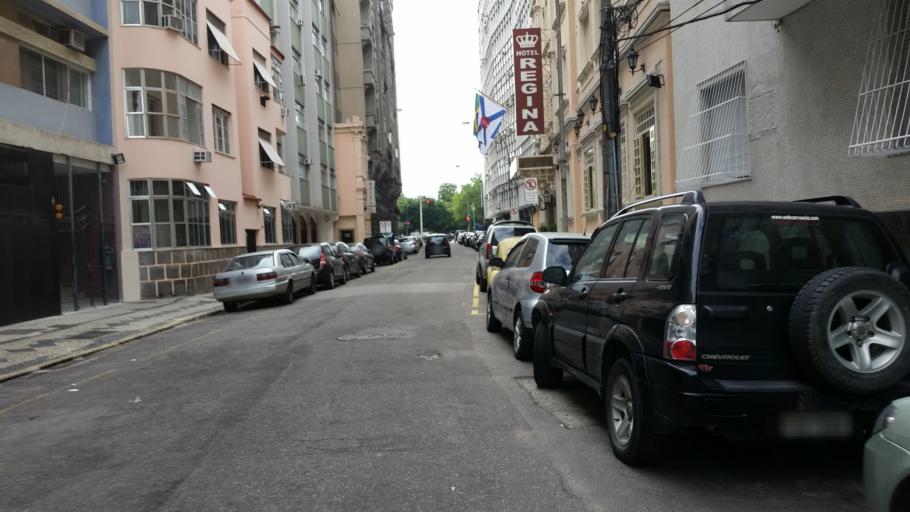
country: BR
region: Rio de Janeiro
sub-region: Rio De Janeiro
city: Rio de Janeiro
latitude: -22.9273
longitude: -43.1749
